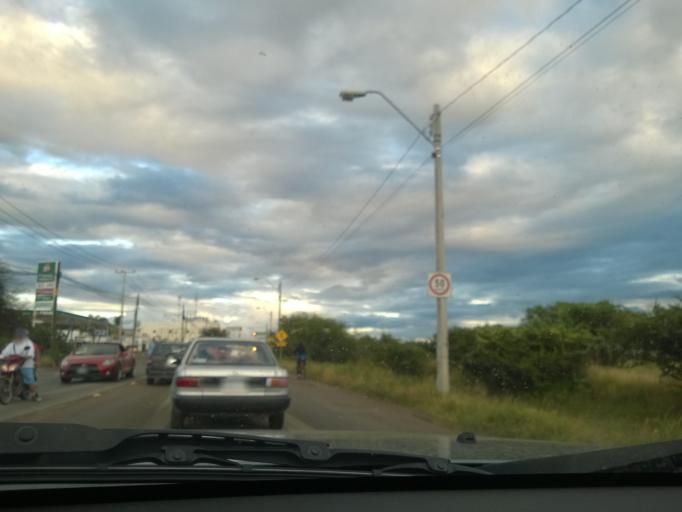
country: MX
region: Guanajuato
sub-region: Leon
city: Fraccionamiento Paraiso Real
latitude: 21.1092
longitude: -101.5937
